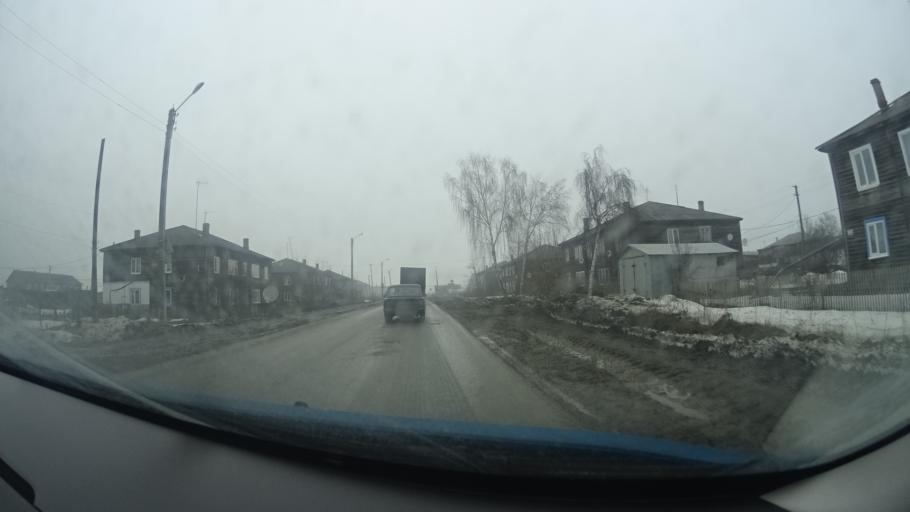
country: RU
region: Perm
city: Kuyeda
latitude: 56.4307
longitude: 55.5770
